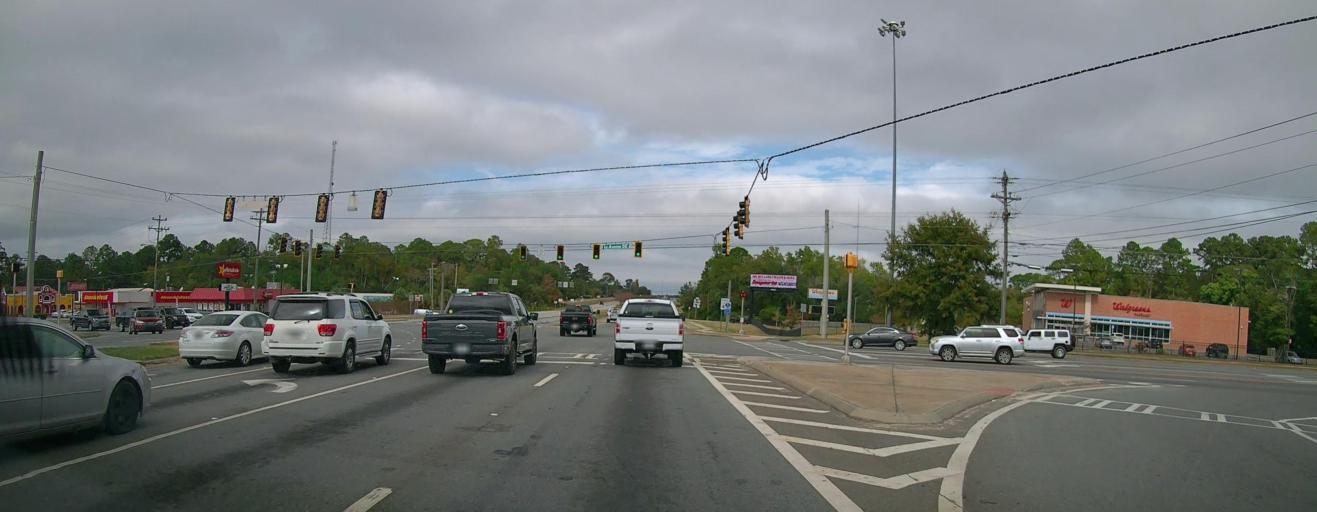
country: US
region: Georgia
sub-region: Colquitt County
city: Moultrie
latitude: 31.1760
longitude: -83.7615
